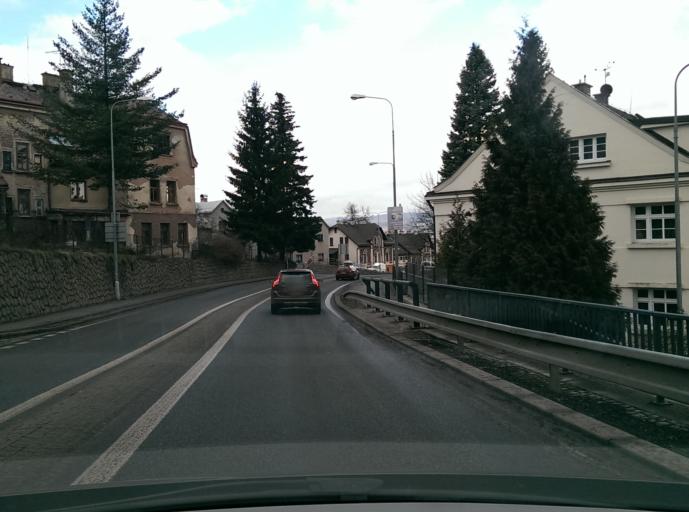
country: CZ
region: Liberecky
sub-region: Okres Jablonec nad Nisou
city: Jablonec nad Nisou
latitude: 50.7178
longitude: 15.1630
